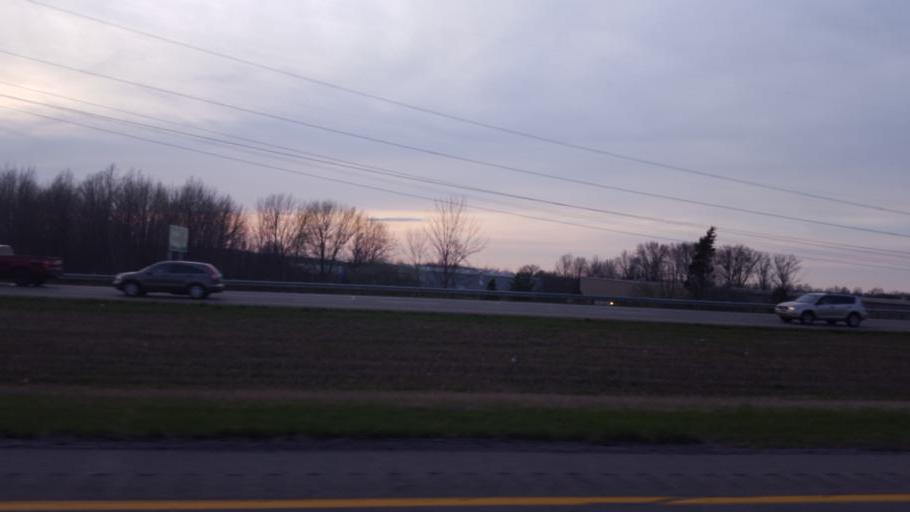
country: US
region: Ohio
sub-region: Lorain County
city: Avon
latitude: 41.4509
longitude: -82.0695
